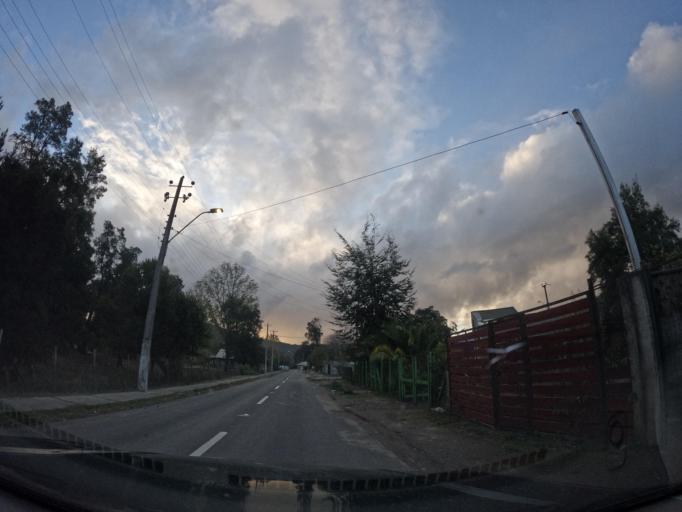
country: CL
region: Biobio
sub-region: Provincia de Concepcion
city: Chiguayante
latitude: -37.0553
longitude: -72.9598
